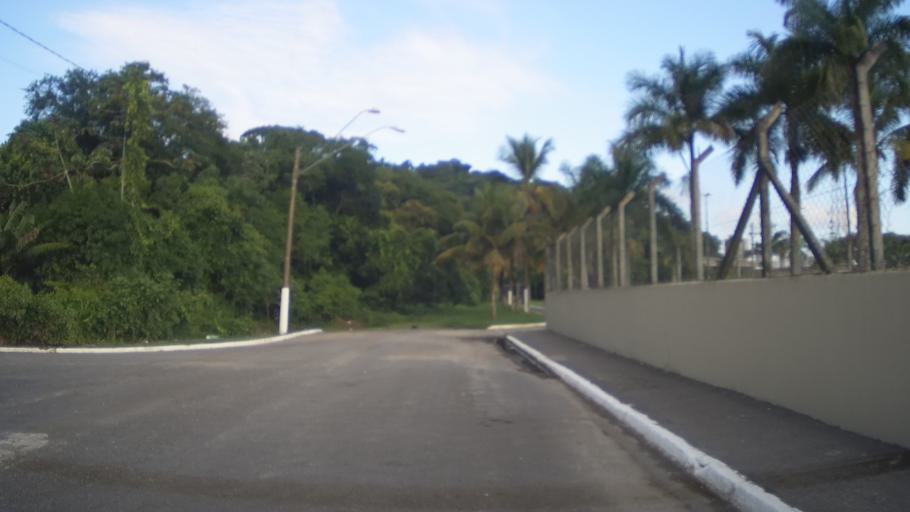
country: BR
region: Sao Paulo
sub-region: Praia Grande
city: Praia Grande
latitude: -23.9967
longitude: -46.4136
